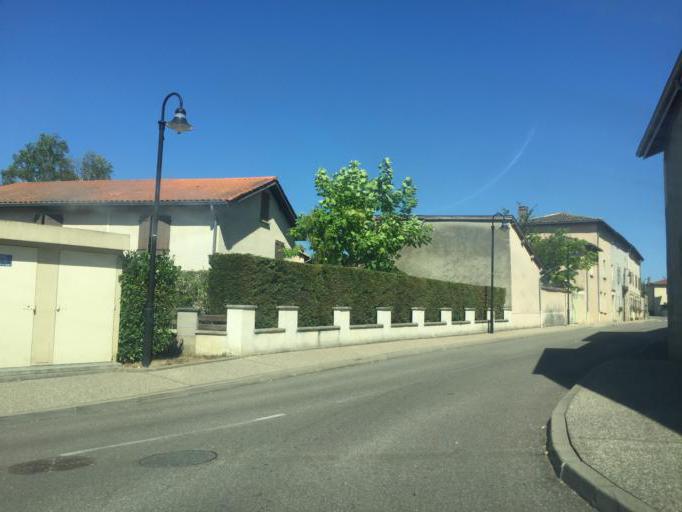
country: FR
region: Rhone-Alpes
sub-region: Departement de l'Ain
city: Tramoyes
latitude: 45.8766
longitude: 4.9682
